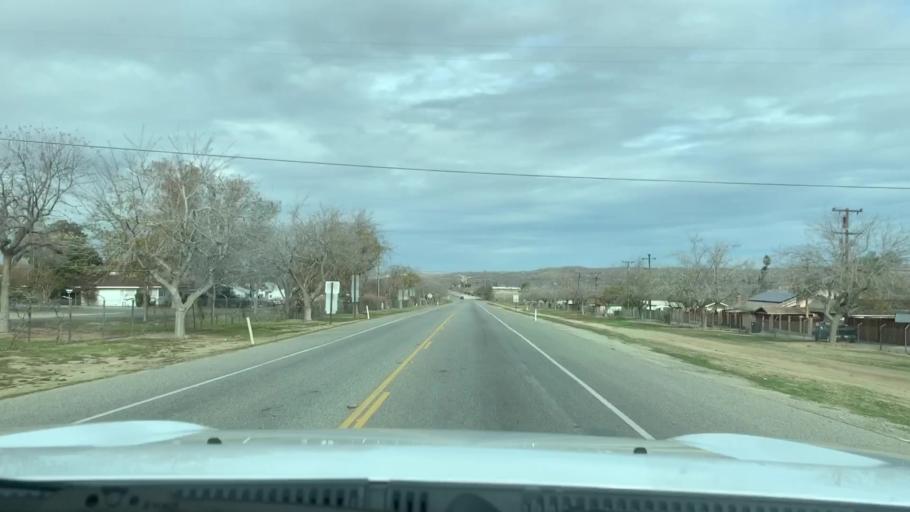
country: US
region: California
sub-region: Kern County
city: Taft
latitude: 35.1411
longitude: -119.4472
